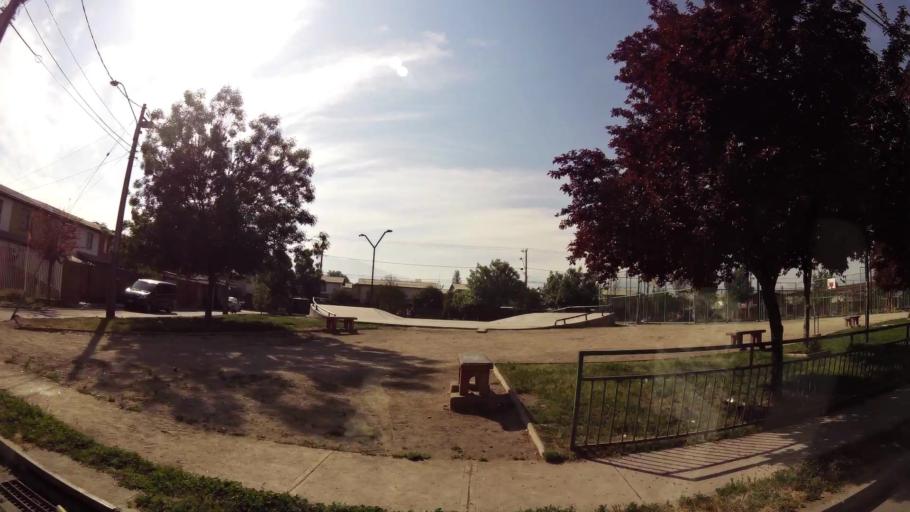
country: CL
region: Santiago Metropolitan
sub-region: Provincia de Santiago
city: La Pintana
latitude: -33.5620
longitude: -70.6338
